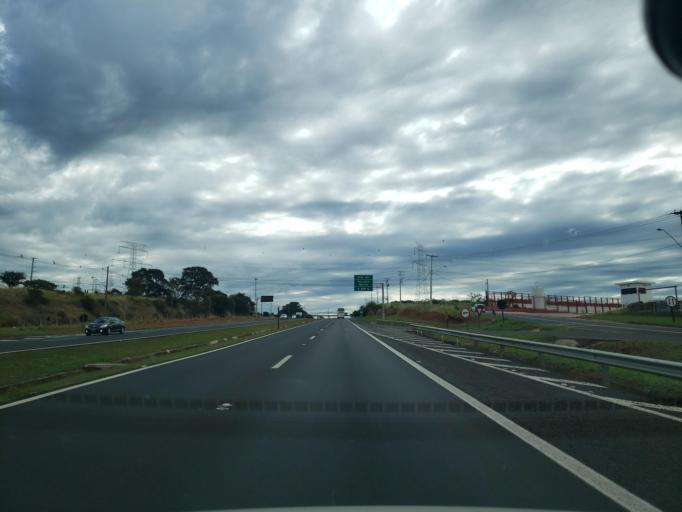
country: BR
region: Sao Paulo
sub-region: Bauru
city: Bauru
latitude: -22.2862
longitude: -49.0814
